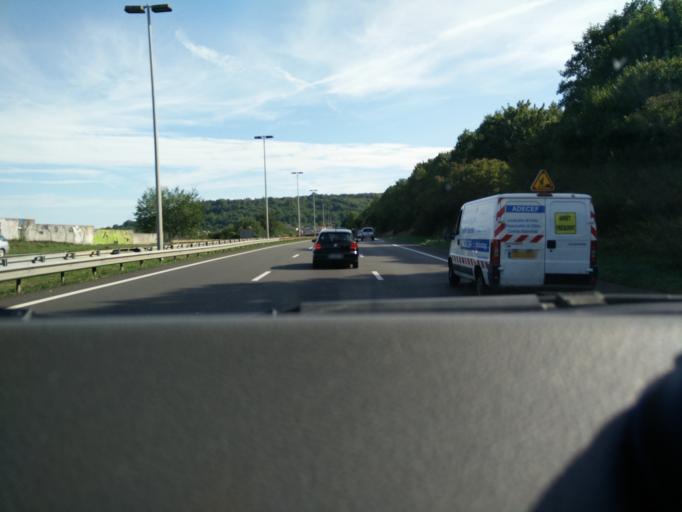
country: FR
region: Lorraine
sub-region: Departement de Meurthe-et-Moselle
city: Champigneulles
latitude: 48.7355
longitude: 6.1571
